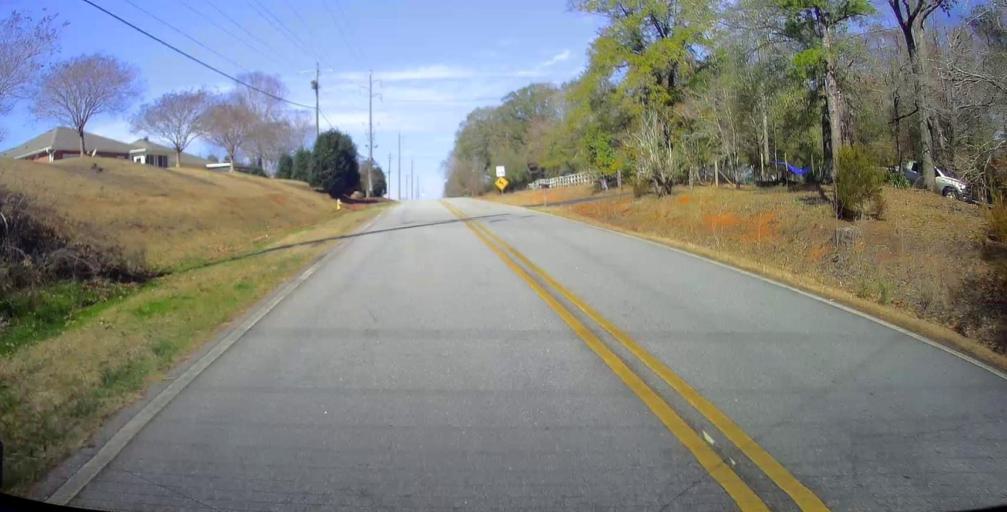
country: US
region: Georgia
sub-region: Houston County
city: Perry
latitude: 32.4720
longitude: -83.7589
